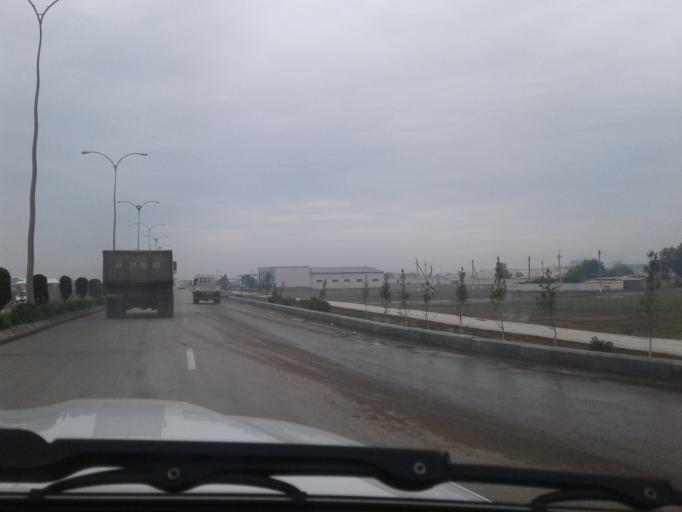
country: TM
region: Mary
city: Bayramaly
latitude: 37.6256
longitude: 62.1436
